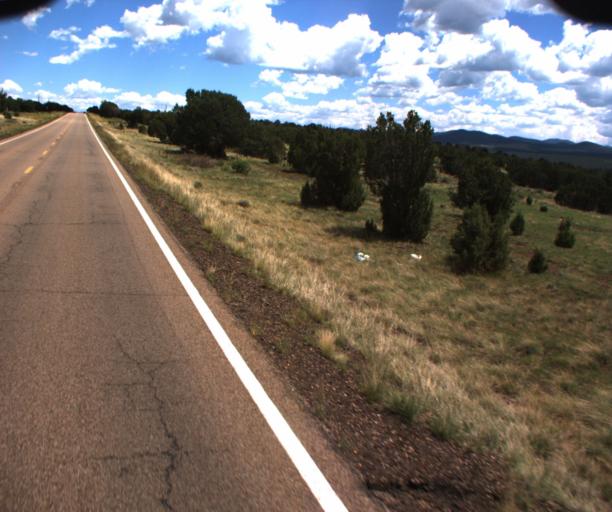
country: US
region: Arizona
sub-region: Navajo County
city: White Mountain Lake
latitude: 34.2838
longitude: -109.8161
